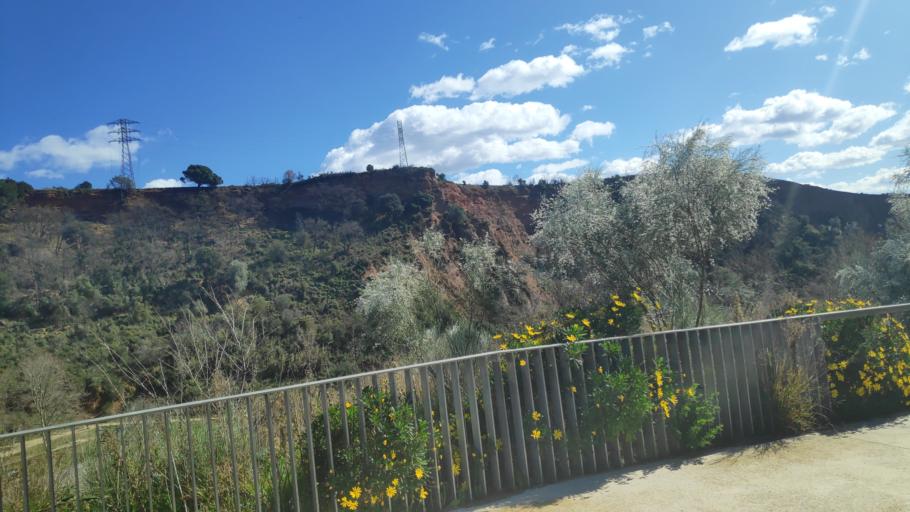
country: ES
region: Catalonia
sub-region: Provincia de Barcelona
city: Sabadell
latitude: 41.5654
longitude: 2.1087
